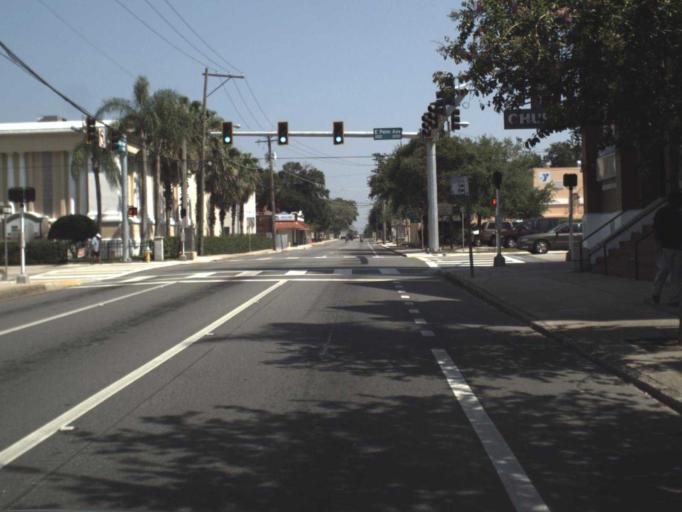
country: US
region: Florida
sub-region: Hillsborough County
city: Tampa
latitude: 27.9619
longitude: -82.4595
